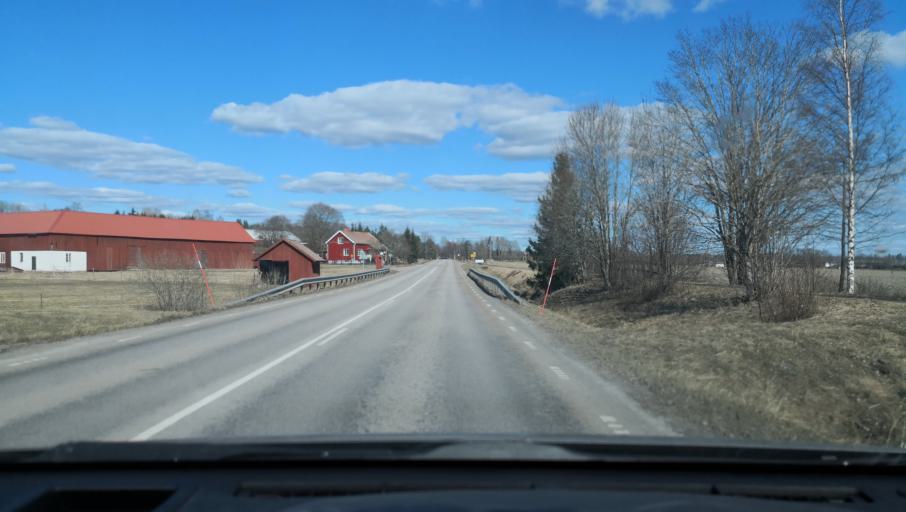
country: SE
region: Vaestmanland
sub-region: Sala Kommun
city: Sala
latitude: 59.9760
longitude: 16.6253
